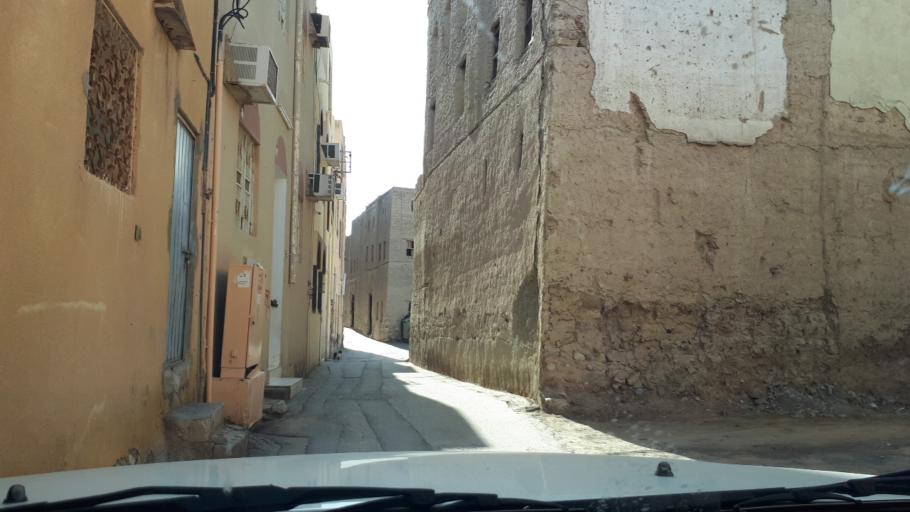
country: OM
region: Muhafazat ad Dakhiliyah
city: Nizwa
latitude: 22.9314
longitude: 57.5312
